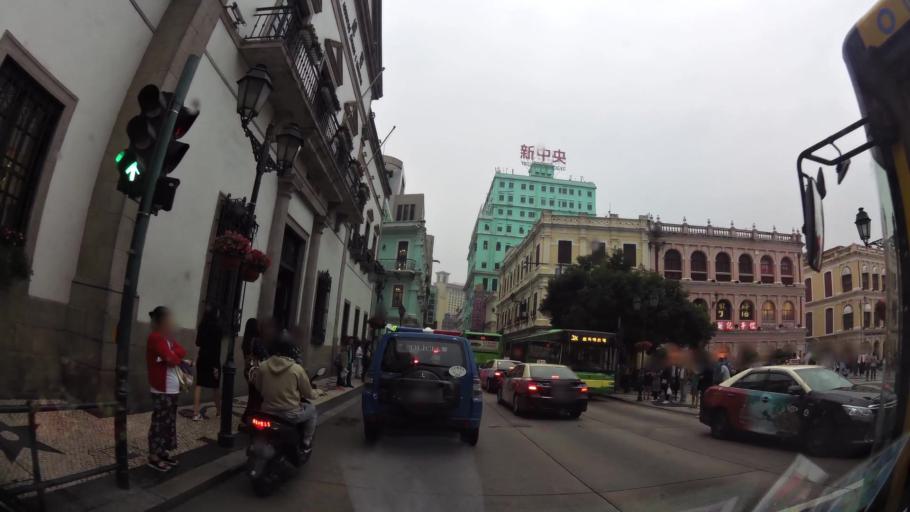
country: MO
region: Macau
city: Macau
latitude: 22.1933
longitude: 113.5398
